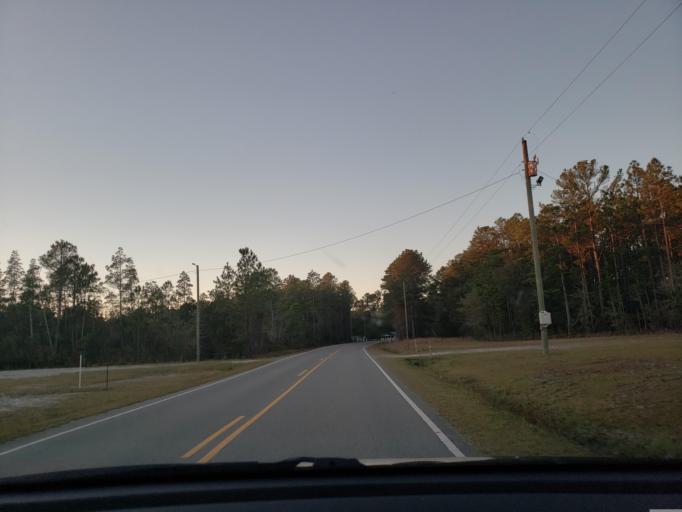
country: US
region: North Carolina
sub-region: Onslow County
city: Richlands
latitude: 34.7248
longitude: -77.6253
